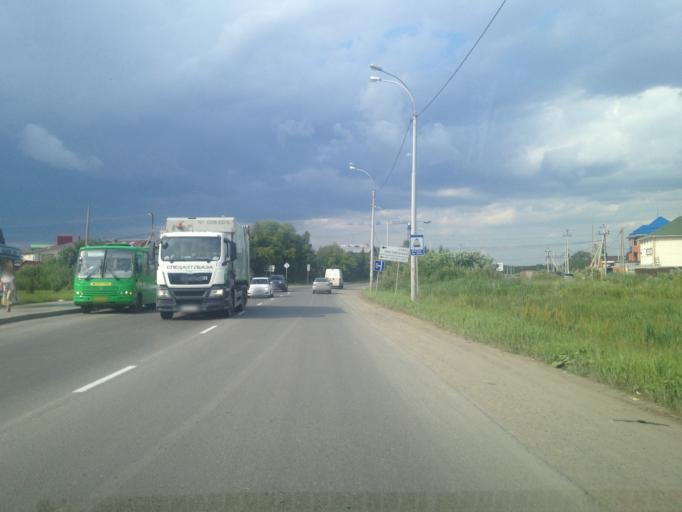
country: RU
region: Sverdlovsk
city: Shirokaya Rechka
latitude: 56.8044
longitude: 60.4946
